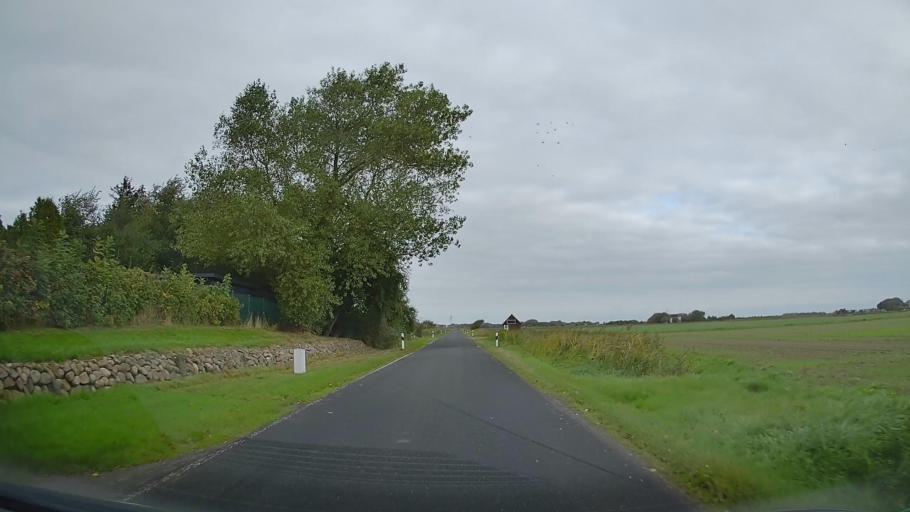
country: DE
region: Schleswig-Holstein
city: Emmelsbull-Horsbull
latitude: 54.8173
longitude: 8.6522
